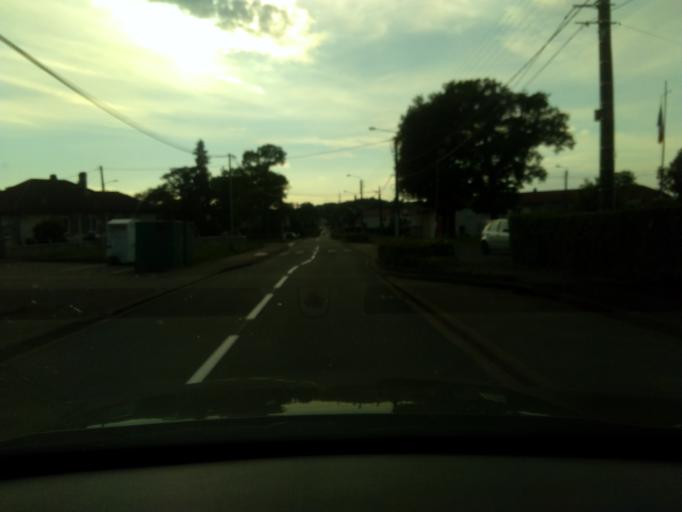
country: FR
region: Lorraine
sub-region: Departement de la Moselle
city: Seremange-Erzange
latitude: 49.3136
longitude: 6.0822
